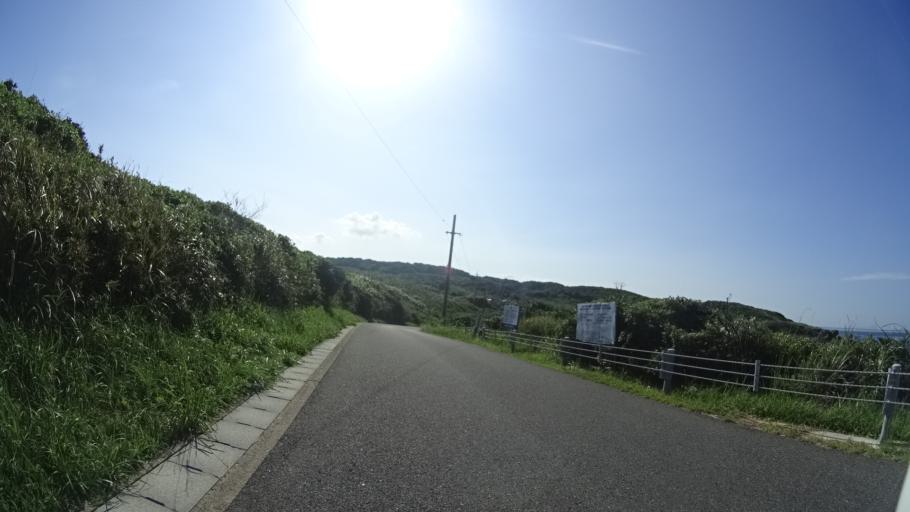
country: JP
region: Yamaguchi
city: Nagato
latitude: 34.3510
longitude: 130.8389
